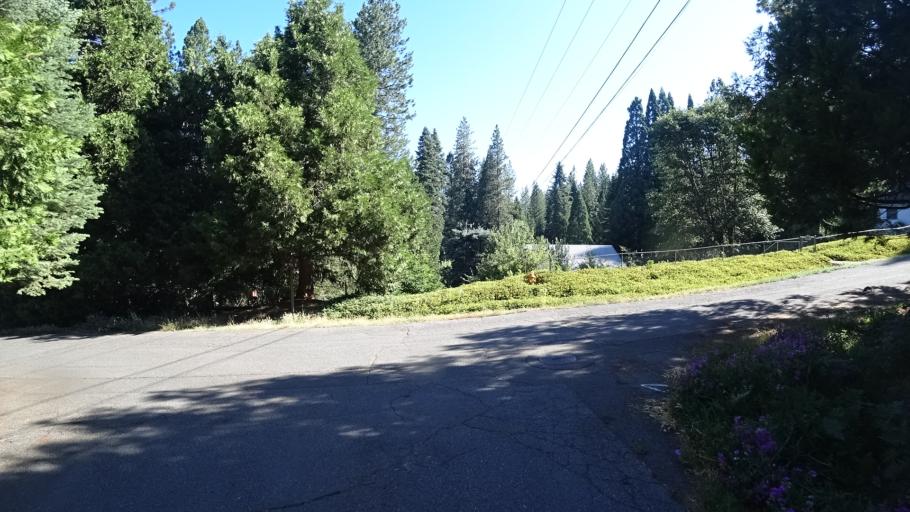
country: US
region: California
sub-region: Calaveras County
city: Arnold
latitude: 38.2656
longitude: -120.3403
